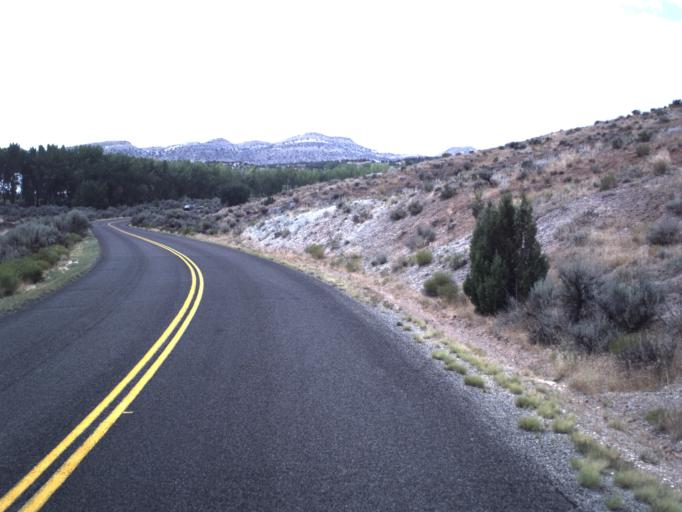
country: US
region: Utah
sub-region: Uintah County
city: Maeser
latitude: 40.5252
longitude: -109.5374
